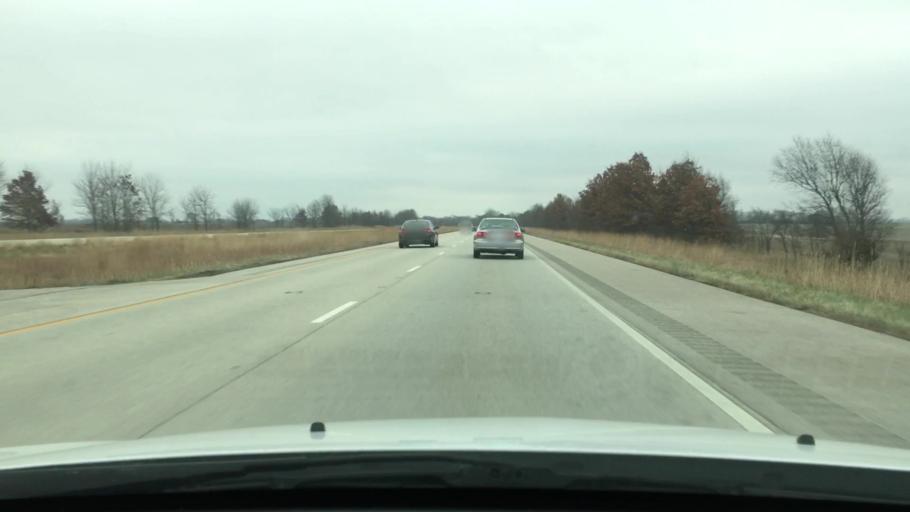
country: US
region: Illinois
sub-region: Sangamon County
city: New Berlin
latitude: 39.7410
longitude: -89.8369
